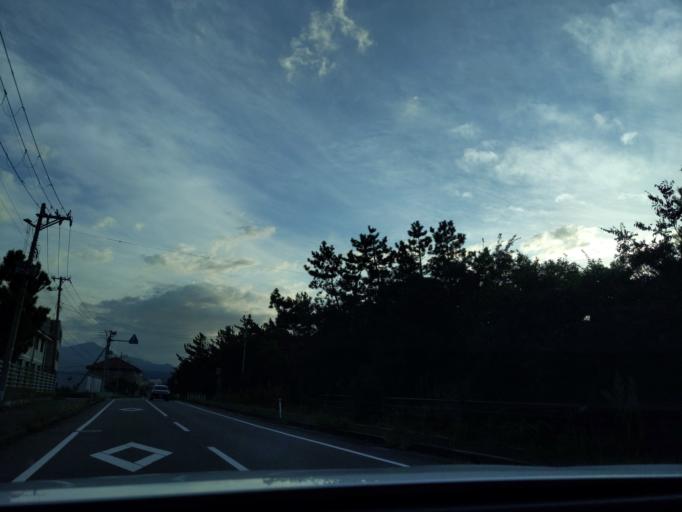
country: JP
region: Niigata
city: Kashiwazaki
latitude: 37.3776
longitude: 138.5562
